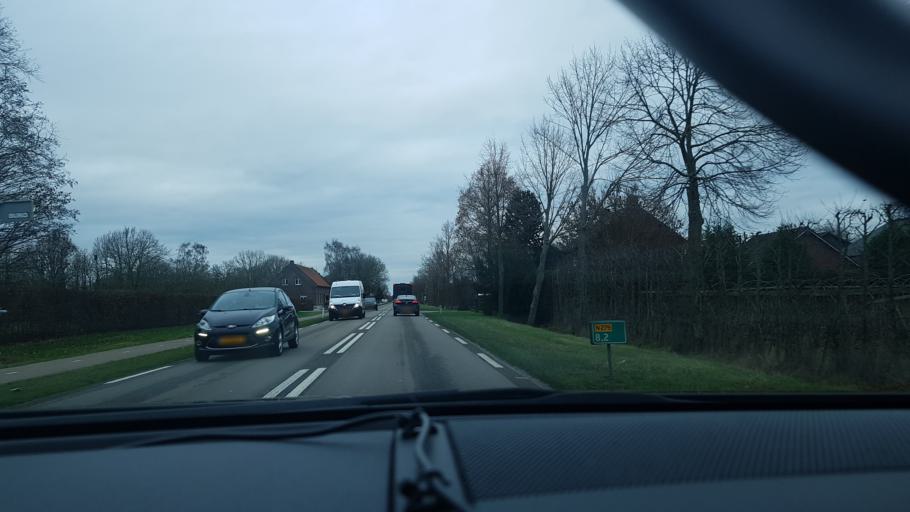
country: NL
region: Limburg
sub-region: Gemeente Leudal
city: Heythuysen
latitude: 51.2727
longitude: 5.9146
